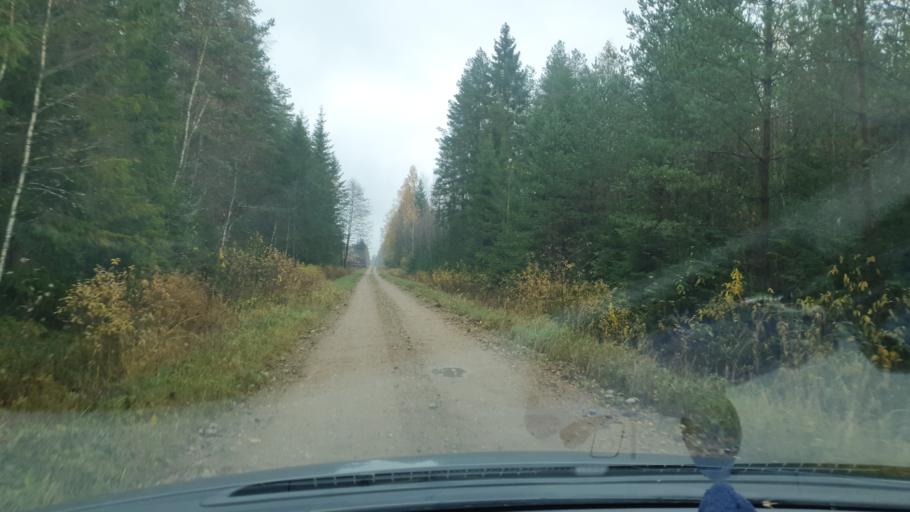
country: EE
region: Viljandimaa
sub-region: Karksi vald
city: Karksi-Nuia
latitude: 57.9797
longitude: 25.6277
